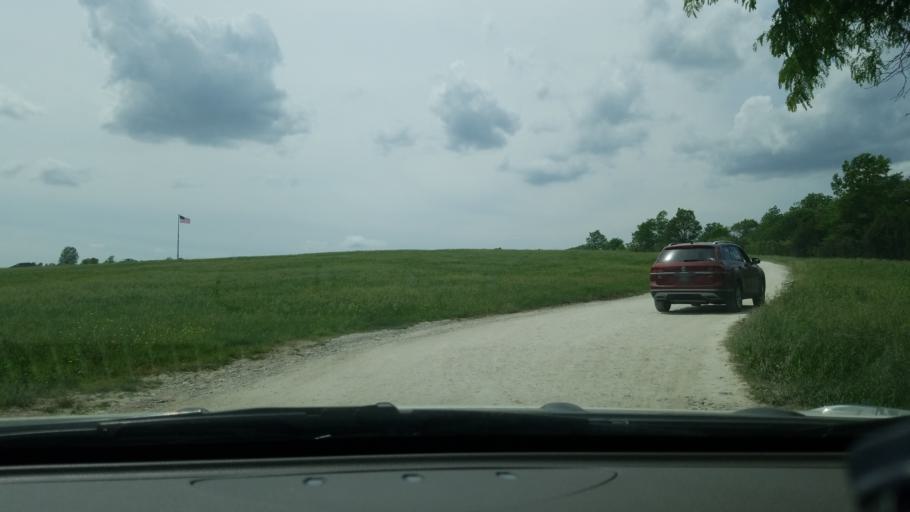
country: US
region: Nebraska
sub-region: Saunders County
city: Ashland
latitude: 41.0110
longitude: -96.2959
